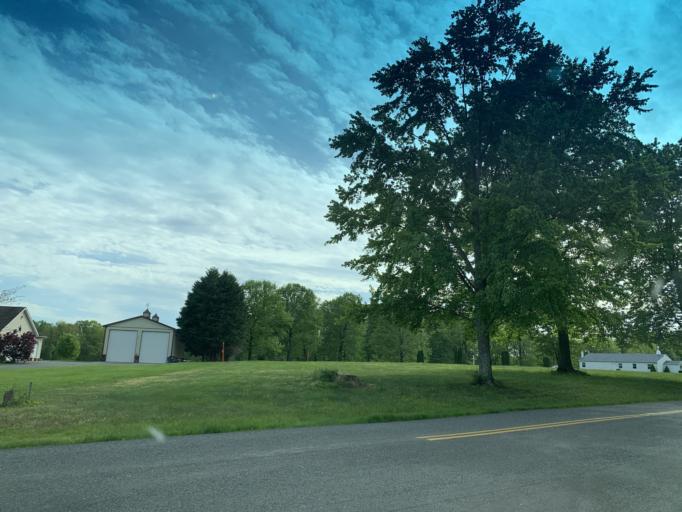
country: US
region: Maryland
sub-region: Harford County
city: South Bel Air
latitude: 39.6377
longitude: -76.2442
